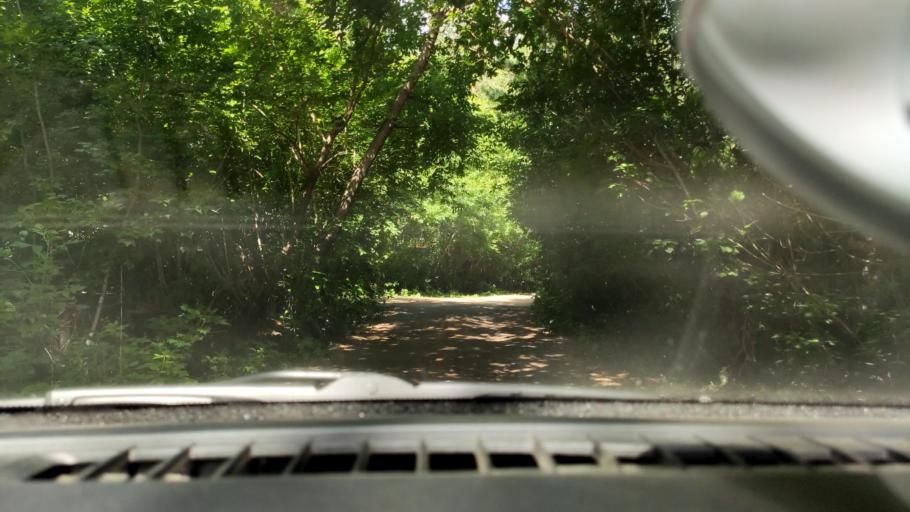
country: RU
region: Samara
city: Samara
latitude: 53.1280
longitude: 50.1782
